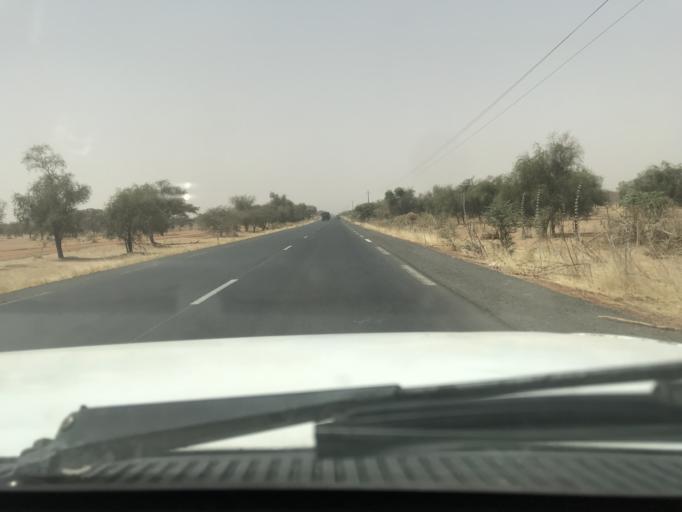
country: SN
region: Louga
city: Ndibene Dahra
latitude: 15.3459
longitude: -15.4354
